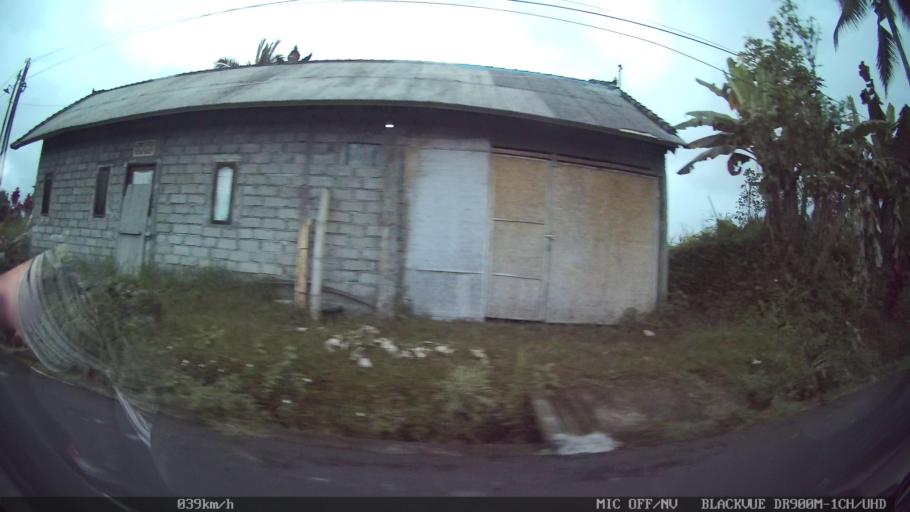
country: ID
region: Bali
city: Peneng
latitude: -8.3596
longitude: 115.1852
